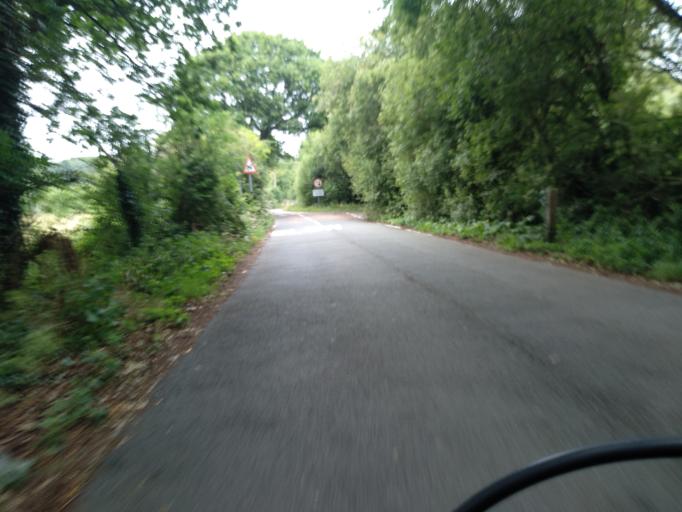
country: GB
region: England
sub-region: Isle of Wight
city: Sandown
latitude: 50.6638
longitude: -1.1692
